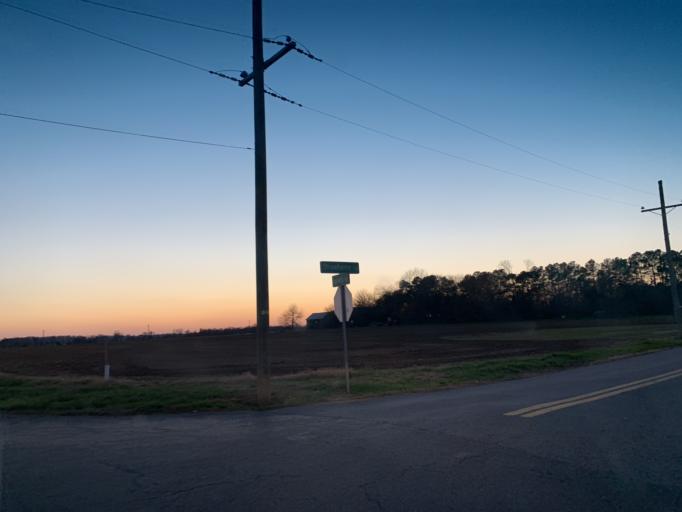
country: US
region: Delaware
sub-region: New Castle County
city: Middletown
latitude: 39.4103
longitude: -75.7489
